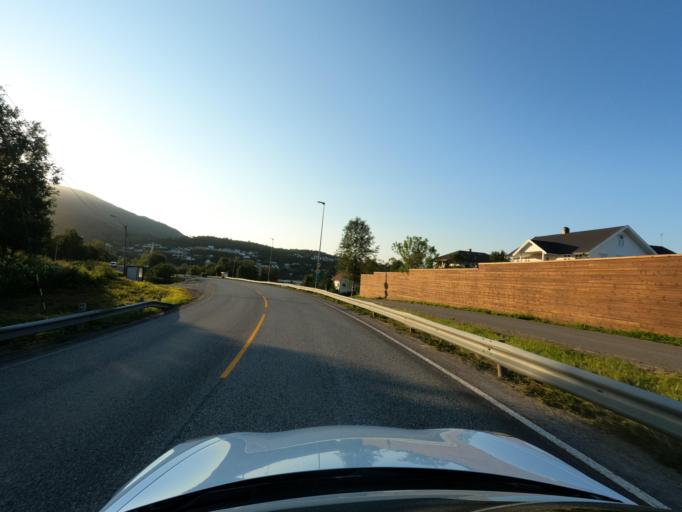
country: NO
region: Troms
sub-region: Harstad
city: Harstad
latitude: 68.7434
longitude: 16.5675
